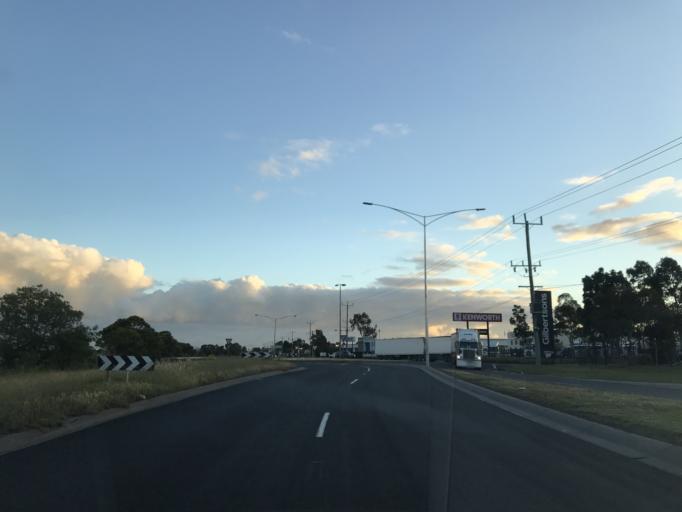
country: AU
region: Victoria
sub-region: Brimbank
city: Derrimut
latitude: -37.8047
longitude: 144.7886
